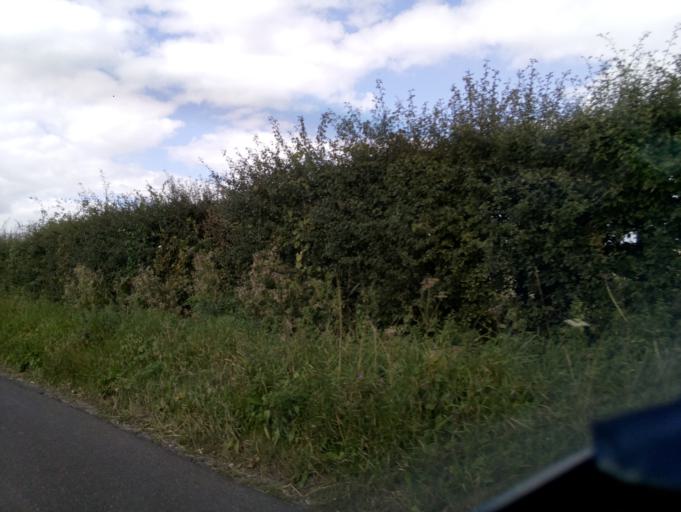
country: GB
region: England
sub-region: Wiltshire
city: Bratton
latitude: 51.2813
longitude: -2.1280
